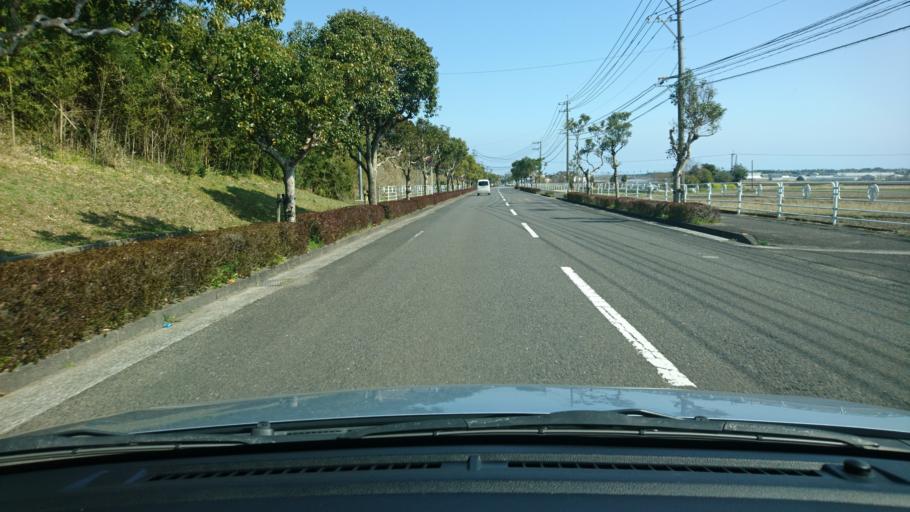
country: JP
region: Miyazaki
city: Miyazaki-shi
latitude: 31.8263
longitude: 131.4296
